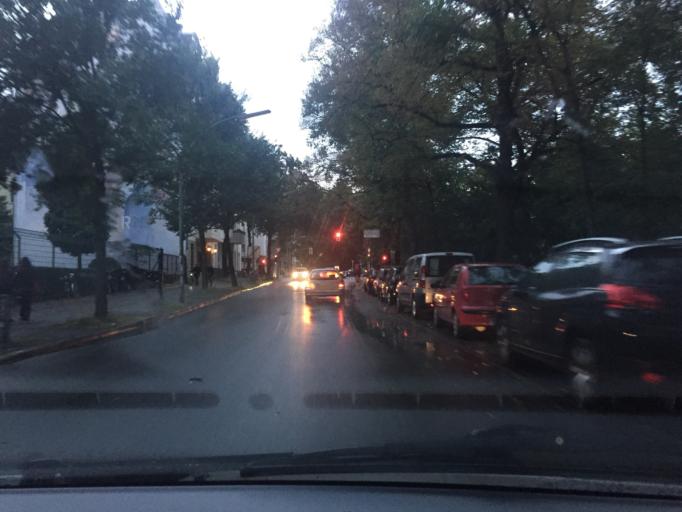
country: DE
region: Berlin
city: Berlin Treptow
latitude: 52.4909
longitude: 13.4364
